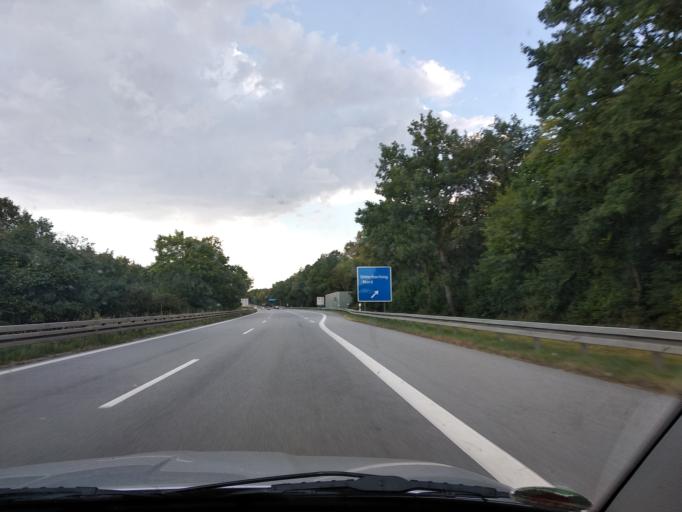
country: DE
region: Bavaria
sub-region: Upper Bavaria
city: Unterhaching
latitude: 48.0763
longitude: 11.5981
